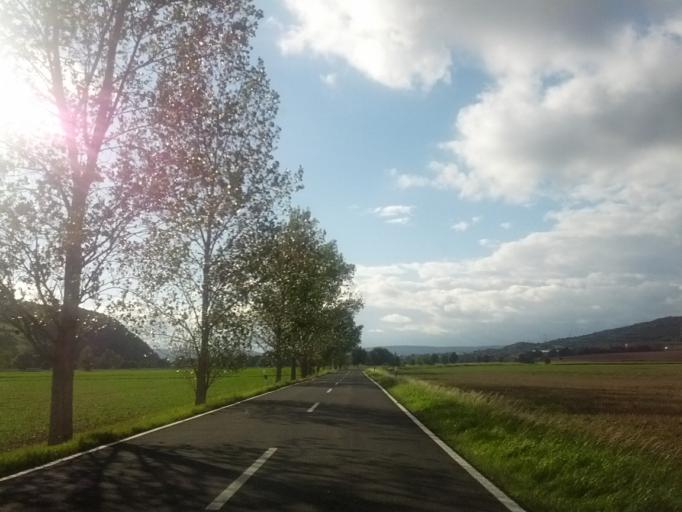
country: DE
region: Hesse
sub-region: Regierungsbezirk Kassel
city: Herleshausen
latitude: 50.9970
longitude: 10.1984
